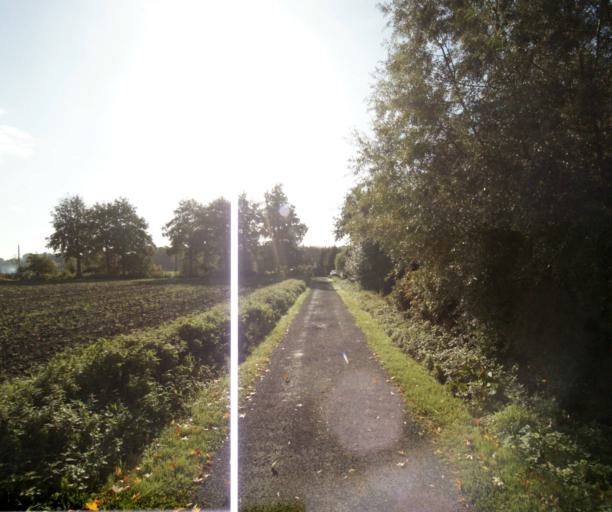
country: FR
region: Nord-Pas-de-Calais
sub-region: Departement du Nord
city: Verlinghem
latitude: 50.6875
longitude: 2.9805
